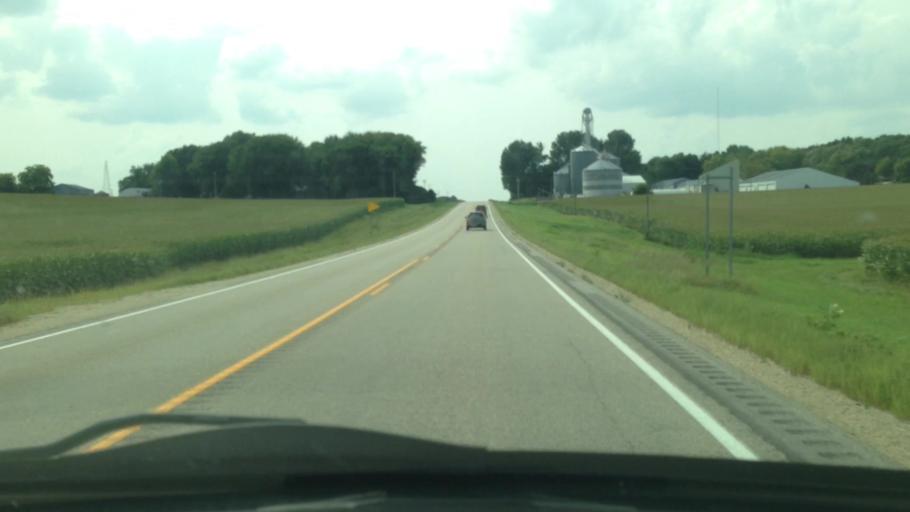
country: US
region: Minnesota
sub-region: Olmsted County
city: Oronoco
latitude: 44.1658
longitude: -92.3955
